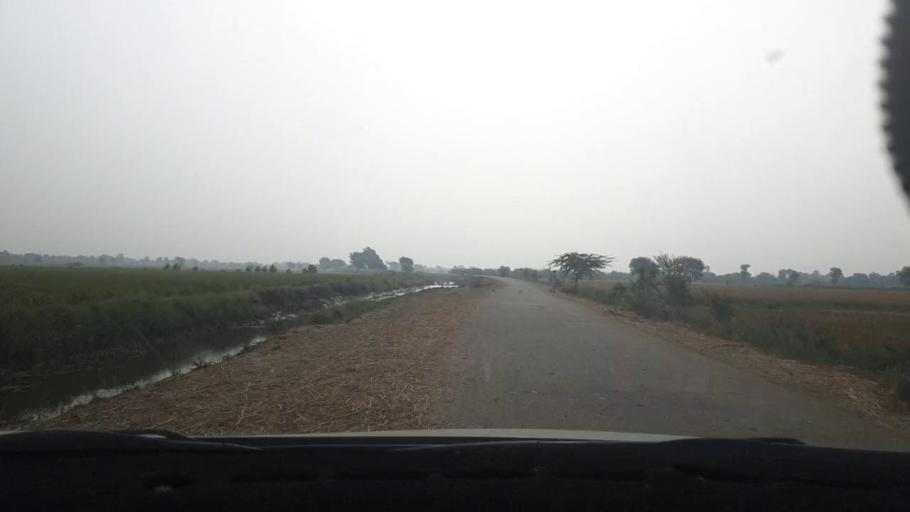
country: PK
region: Sindh
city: Tando Muhammad Khan
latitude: 25.0578
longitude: 68.5459
